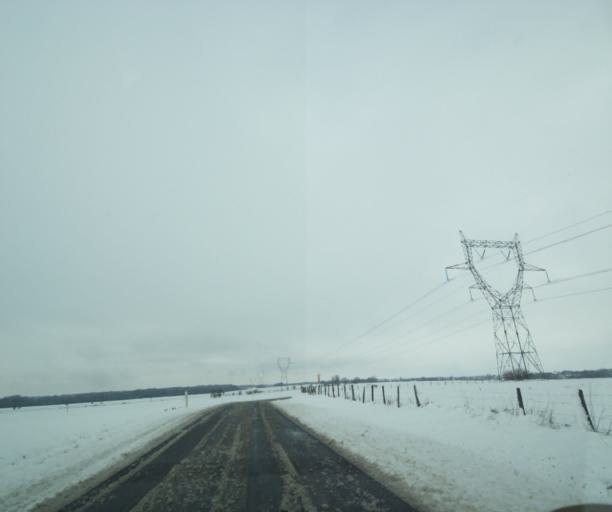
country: FR
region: Champagne-Ardenne
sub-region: Departement de la Haute-Marne
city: Montier-en-Der
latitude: 48.5077
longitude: 4.7211
